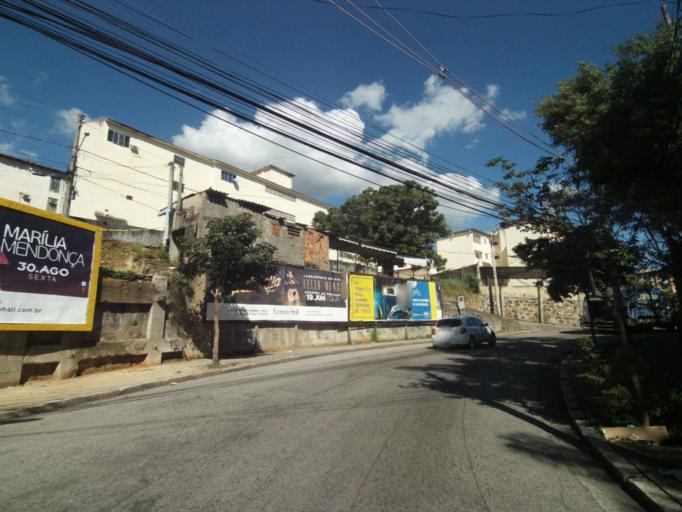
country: BR
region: Rio de Janeiro
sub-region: Rio De Janeiro
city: Rio de Janeiro
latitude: -22.9054
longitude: -43.2736
